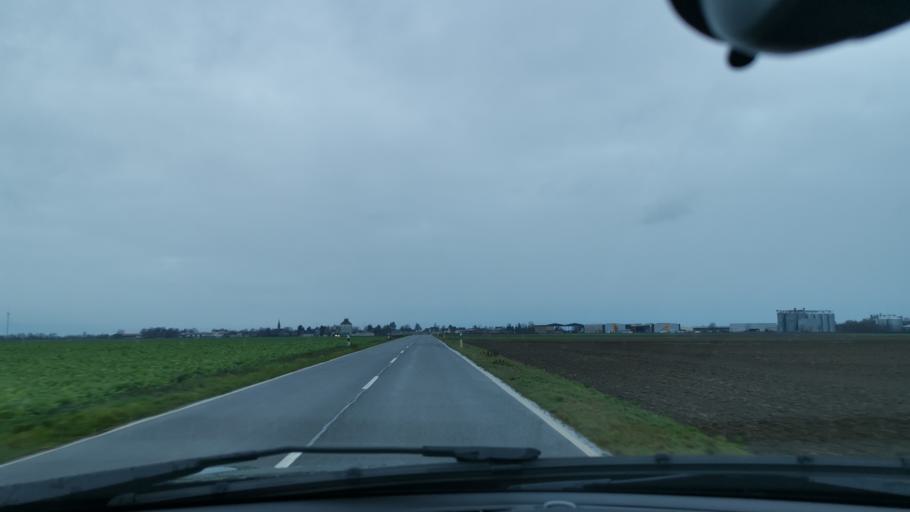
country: DE
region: North Rhine-Westphalia
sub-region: Regierungsbezirk Koln
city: Titz
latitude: 50.9889
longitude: 6.4523
